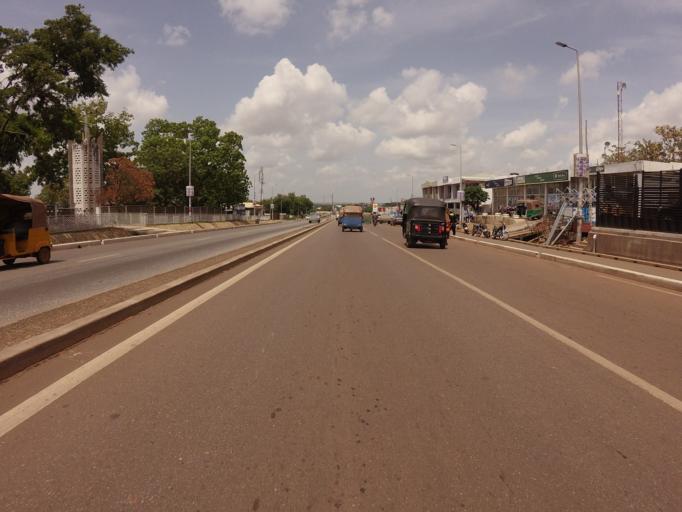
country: GH
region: Northern
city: Tamale
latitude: 9.4007
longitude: -0.8356
